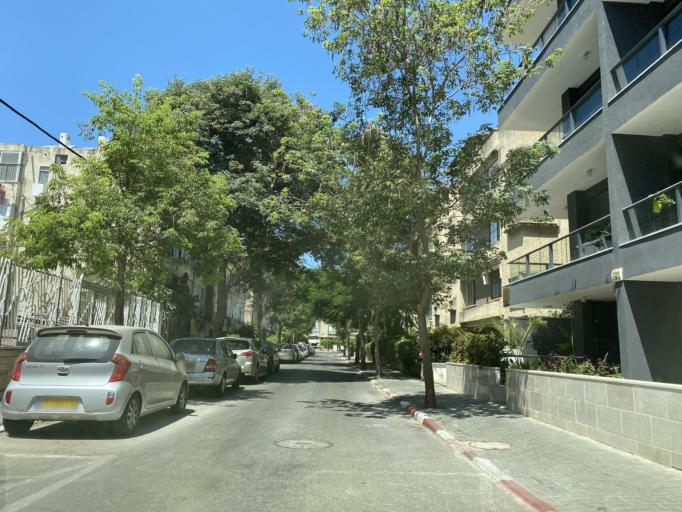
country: IL
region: Tel Aviv
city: Herzliyya
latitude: 32.1654
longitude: 34.8438
